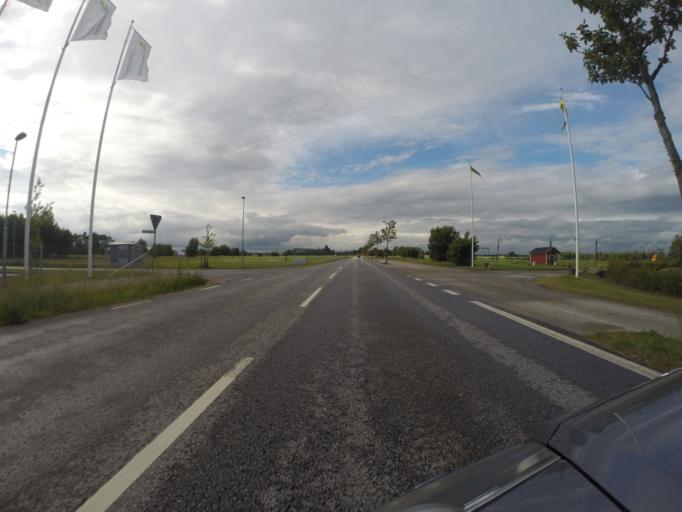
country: SE
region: Skane
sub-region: Kavlinge Kommun
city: Loddekopinge
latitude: 55.7680
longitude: 13.0121
